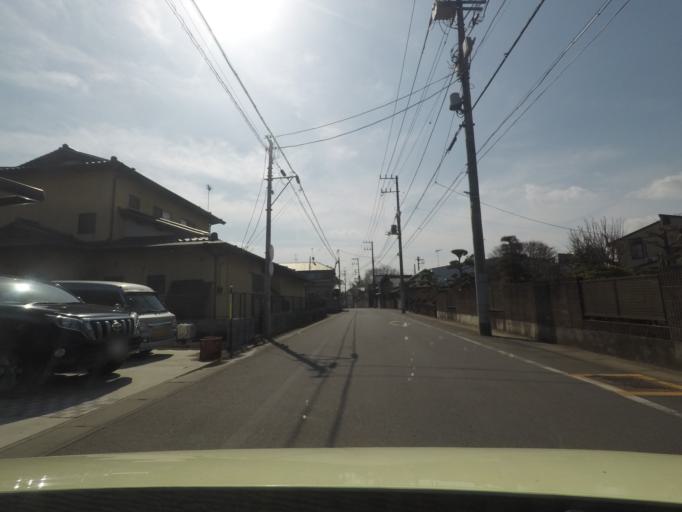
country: JP
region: Ibaraki
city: Ishioka
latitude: 36.1780
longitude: 140.3606
